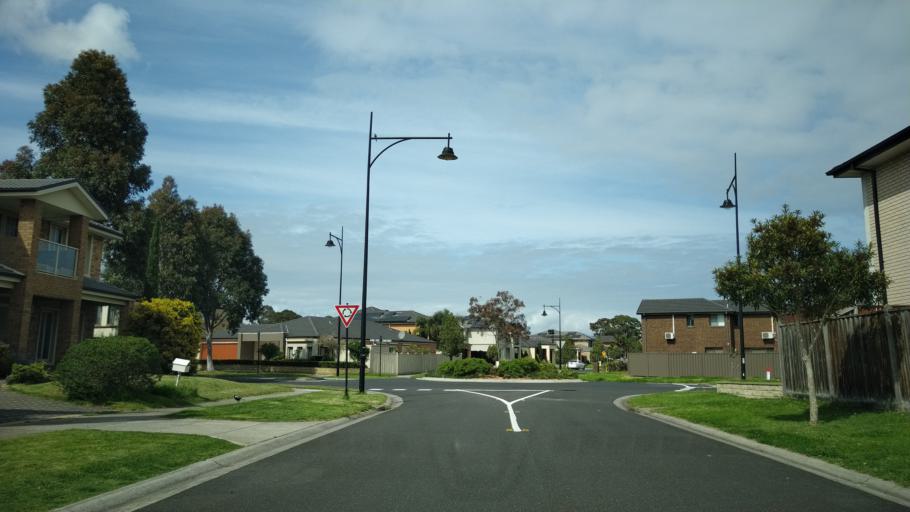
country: AU
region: Victoria
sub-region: Kingston
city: Waterways
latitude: -38.0039
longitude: 145.1491
